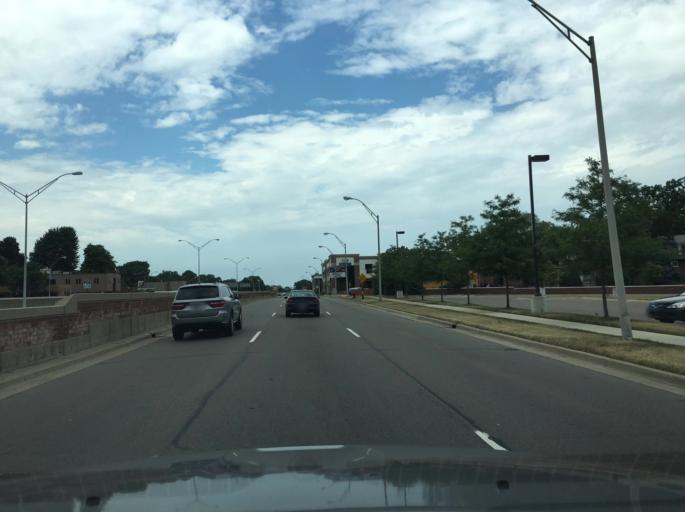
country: US
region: Michigan
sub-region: Oakland County
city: Pleasant Ridge
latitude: 42.4777
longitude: -83.1475
